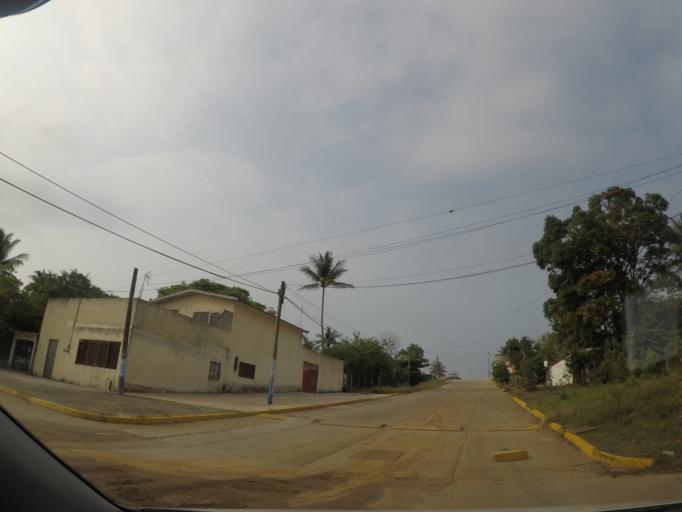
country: MX
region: Oaxaca
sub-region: Santa Maria Petapa
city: Llano Suchiapa
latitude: 16.8701
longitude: -95.0484
